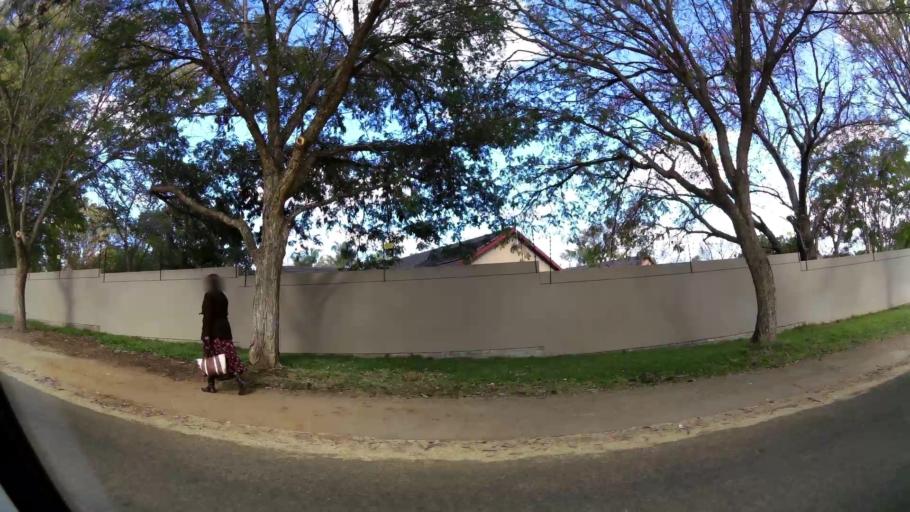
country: ZA
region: Limpopo
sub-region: Capricorn District Municipality
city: Polokwane
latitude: -23.8915
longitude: 29.4785
